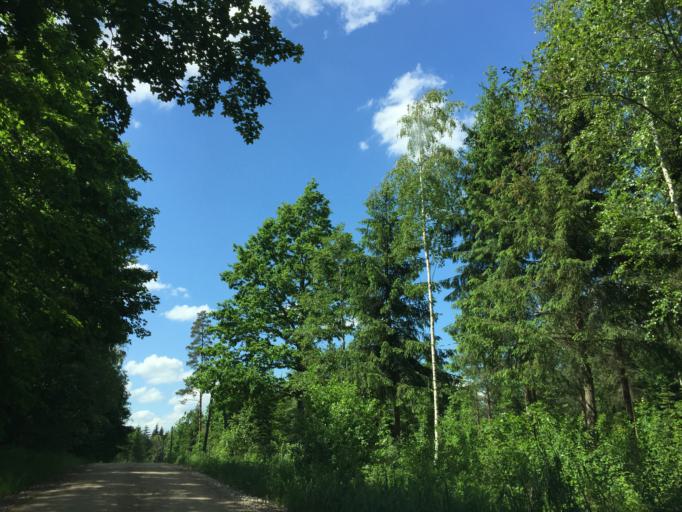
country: LV
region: Priekuli
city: Priekuli
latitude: 57.2294
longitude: 25.4355
